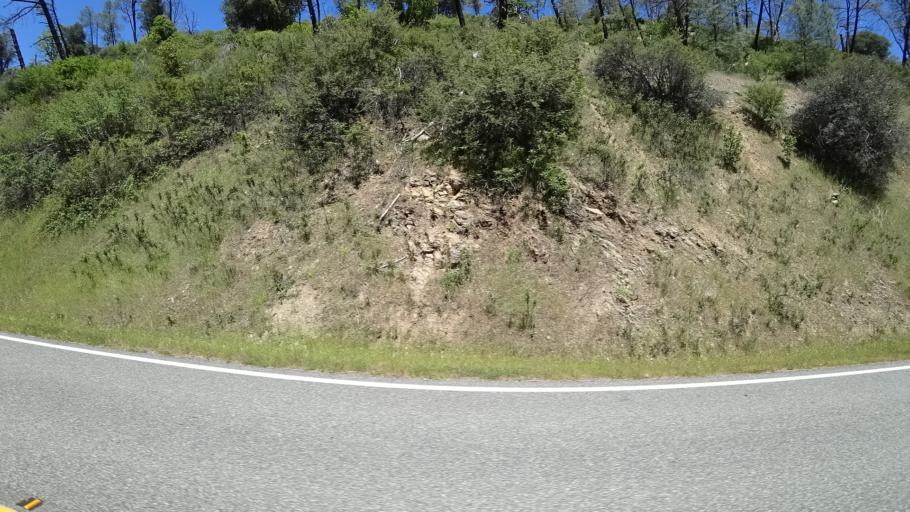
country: US
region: California
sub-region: Trinity County
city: Hayfork
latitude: 40.7358
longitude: -123.2001
